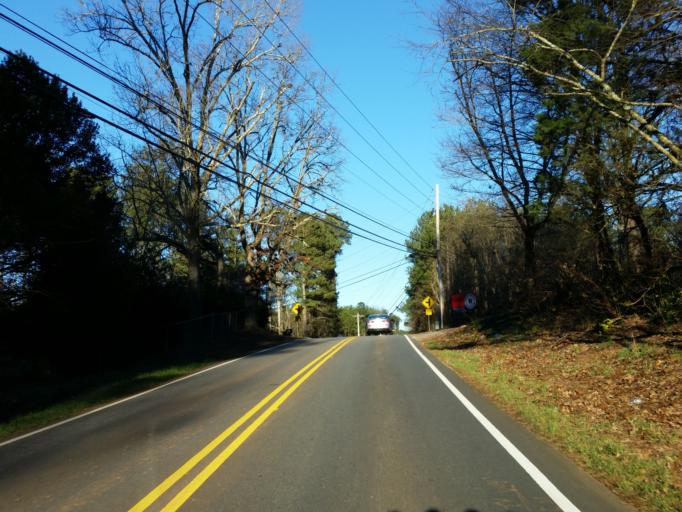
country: US
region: Georgia
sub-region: Cherokee County
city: Woodstock
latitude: 34.1188
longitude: -84.4544
